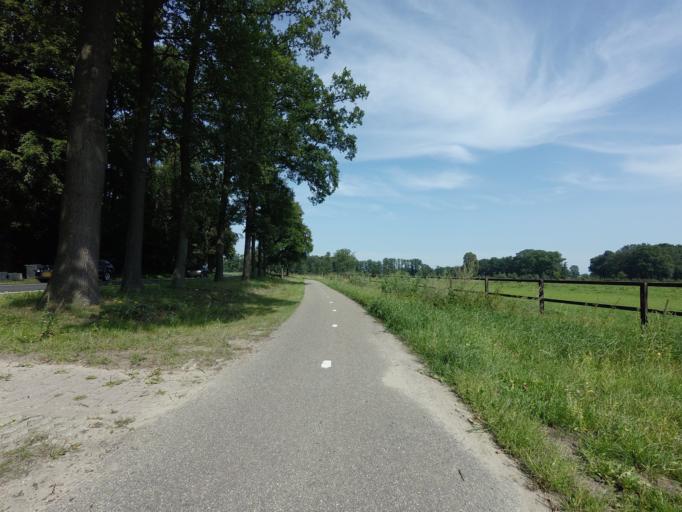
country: NL
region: Overijssel
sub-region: Gemeente Borne
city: Borne
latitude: 52.3316
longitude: 6.7287
